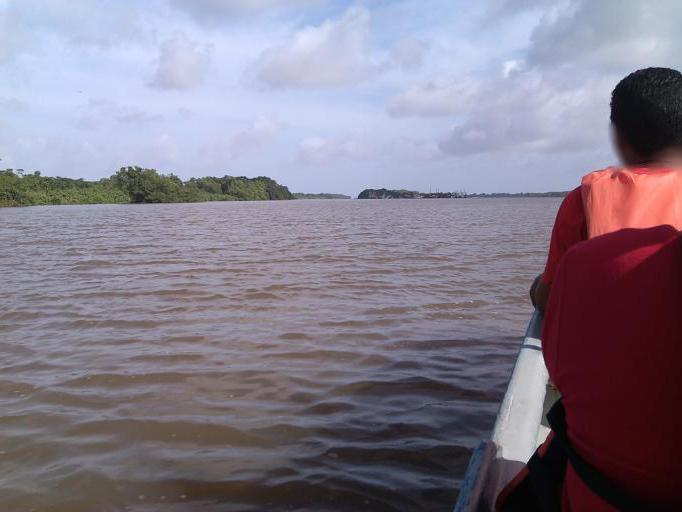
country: NI
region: Atlantico Sur
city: Bluefields
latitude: 12.0870
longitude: -83.7491
